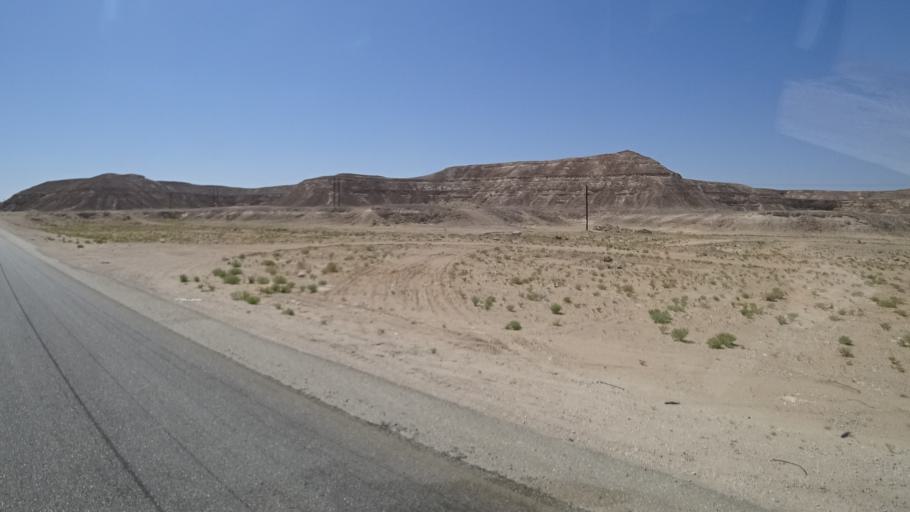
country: OM
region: Zufar
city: Salalah
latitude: 17.5036
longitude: 53.3634
